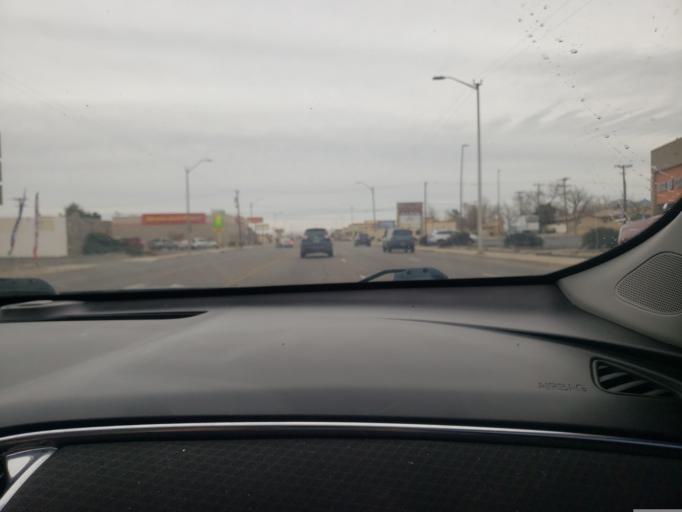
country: US
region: New Mexico
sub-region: Bernalillo County
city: Albuquerque
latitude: 35.1119
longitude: -106.5863
